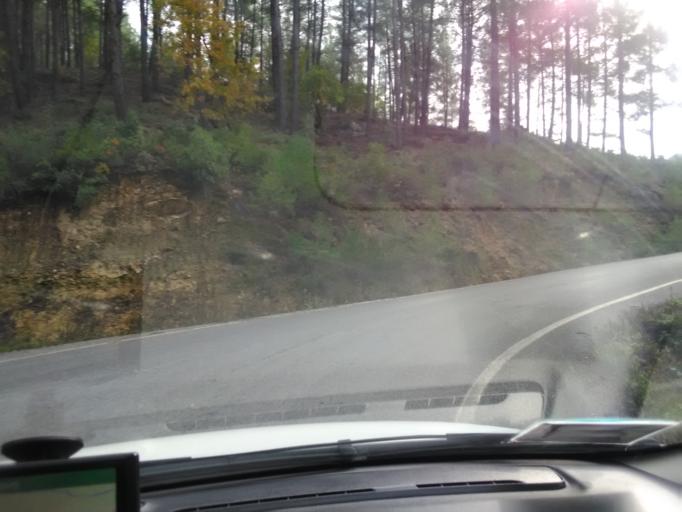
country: TR
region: Antalya
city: Gazipasa
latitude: 36.2455
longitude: 32.4140
